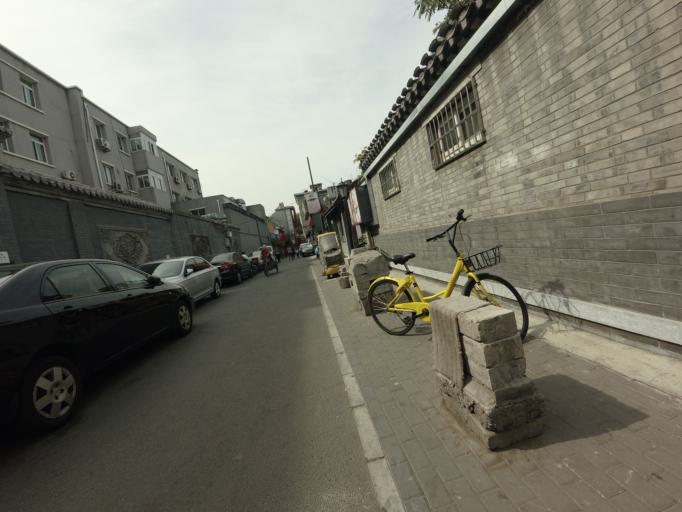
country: CN
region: Beijing
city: Jinrongjie
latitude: 39.9384
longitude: 116.3676
